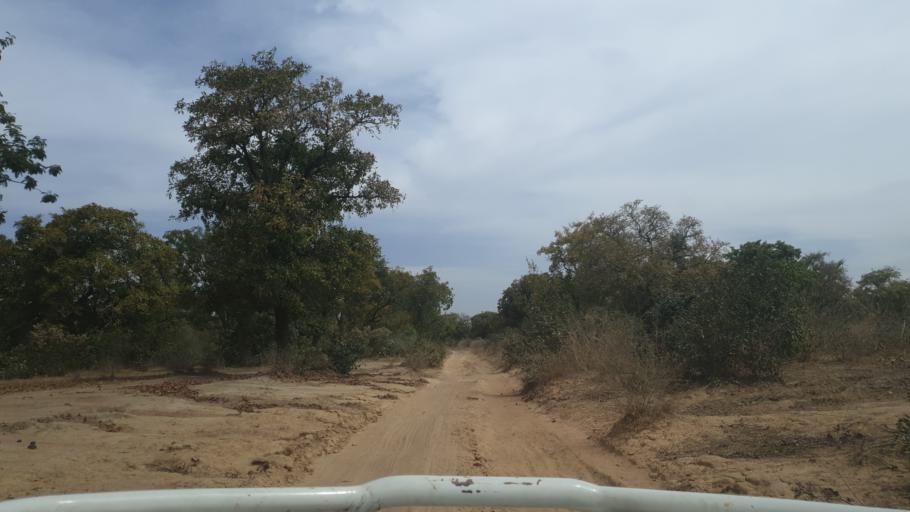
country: ML
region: Sikasso
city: Yorosso
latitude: 12.2445
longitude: -4.7305
